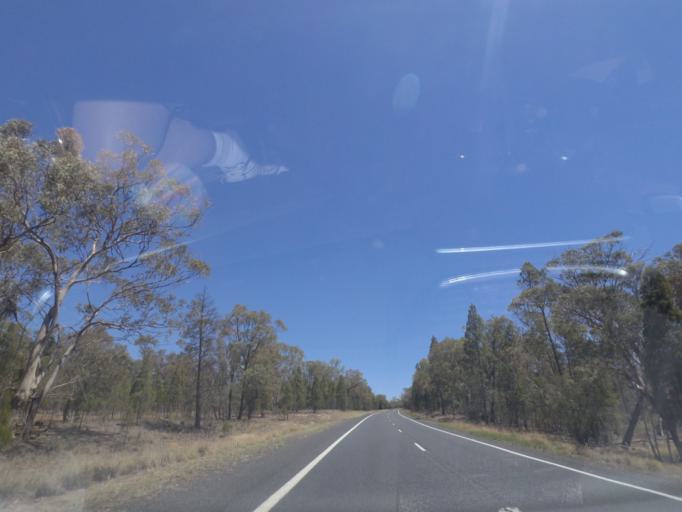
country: AU
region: New South Wales
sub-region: Warrumbungle Shire
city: Coonabarabran
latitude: -31.3343
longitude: 149.3009
